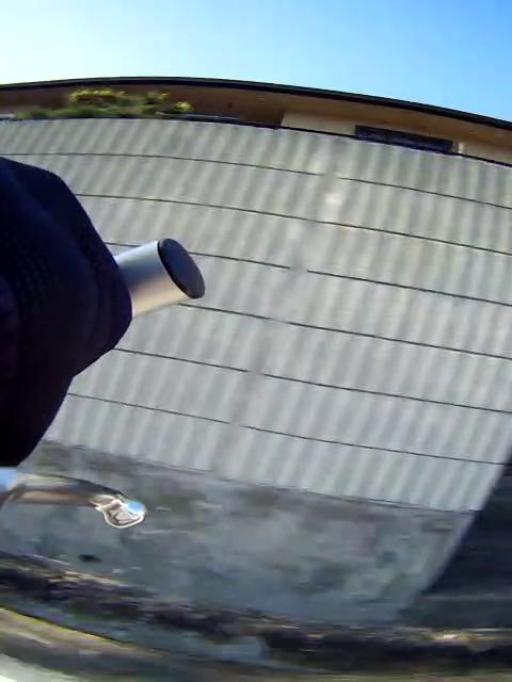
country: JP
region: Hyogo
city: Takarazuka
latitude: 34.7956
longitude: 135.3468
